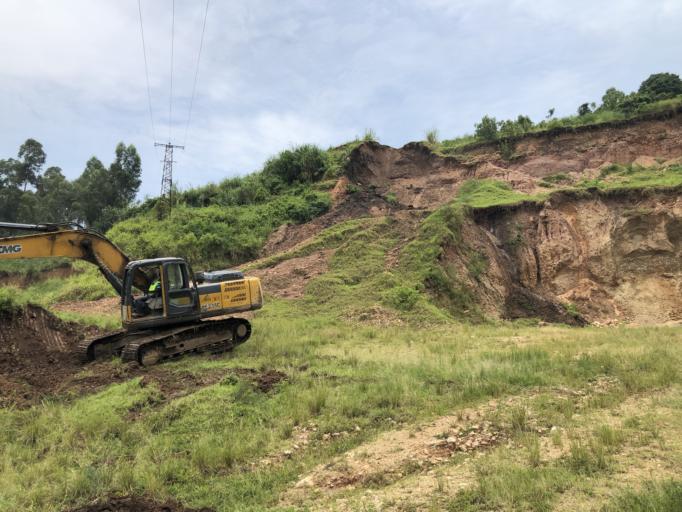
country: CD
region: Nord Kivu
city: Sake
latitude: -1.6723
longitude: 29.0165
